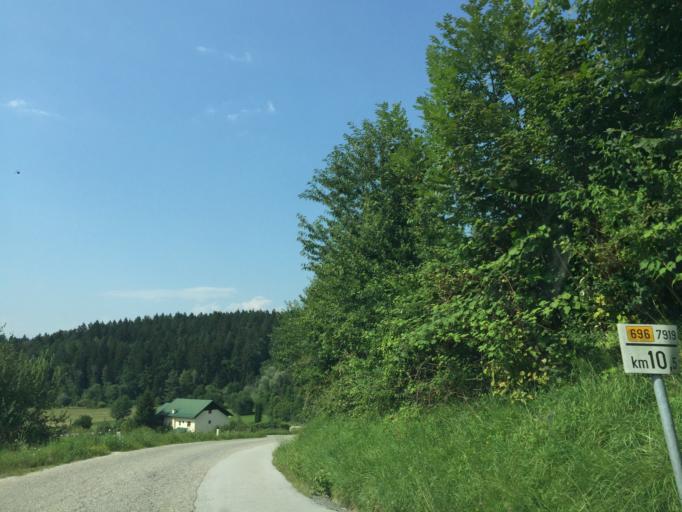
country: SI
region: Slovenj Gradec
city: Smartno pri Slovenj Gradcu
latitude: 46.4525
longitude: 15.1199
